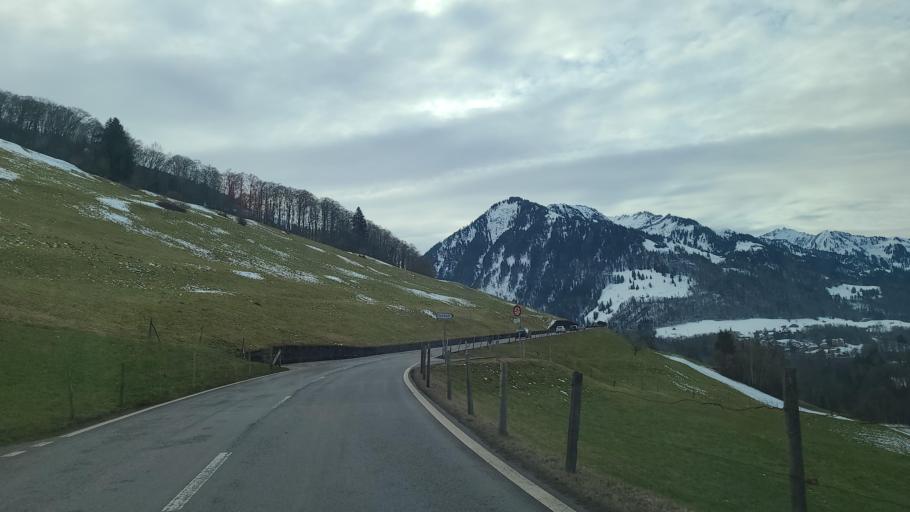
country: CH
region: Obwalden
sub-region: Obwalden
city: Kerns
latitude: 46.8872
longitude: 8.2781
